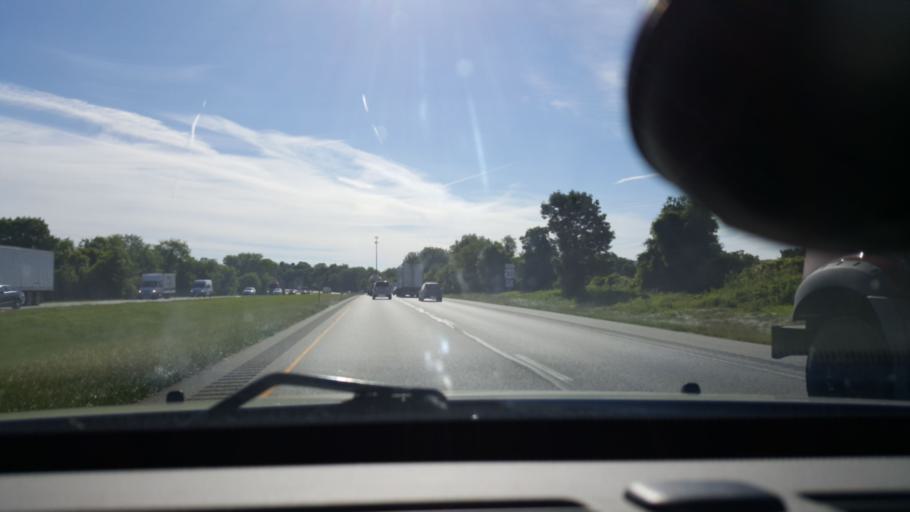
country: US
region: Pennsylvania
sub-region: York County
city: Hallam
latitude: 40.0068
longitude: -76.6108
